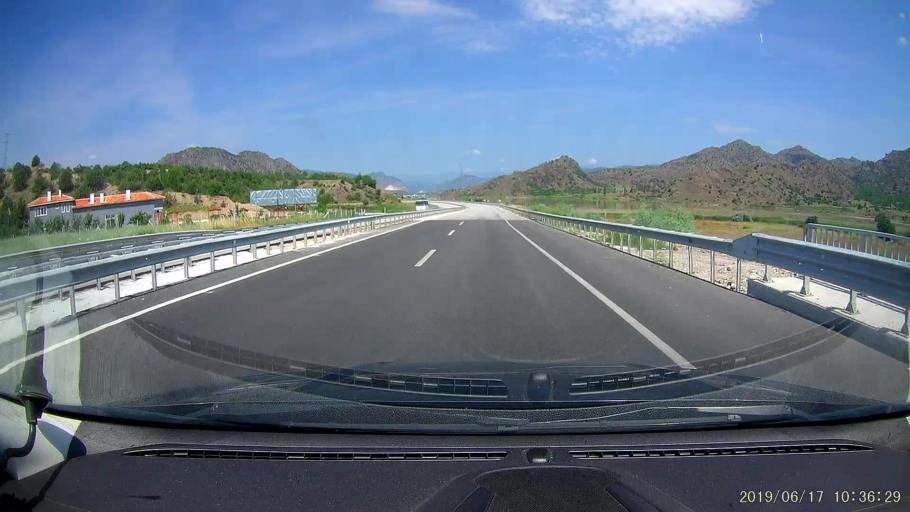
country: TR
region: Corum
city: Osmancik
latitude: 40.9798
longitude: 34.6801
